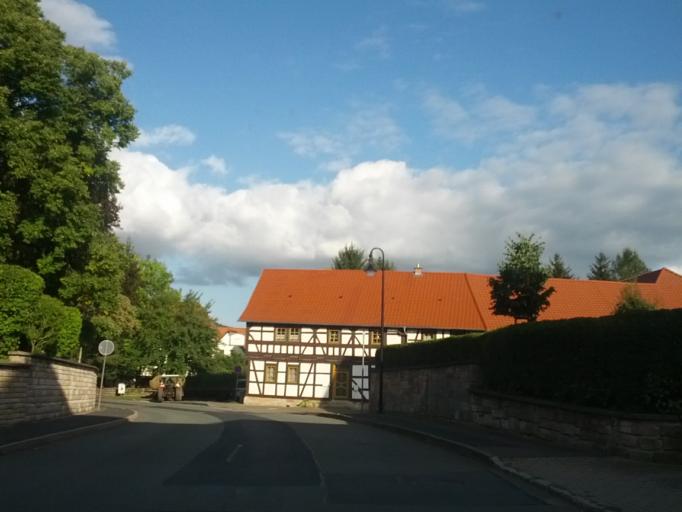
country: DE
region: Thuringia
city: Marksuhl
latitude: 50.9490
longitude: 10.1846
